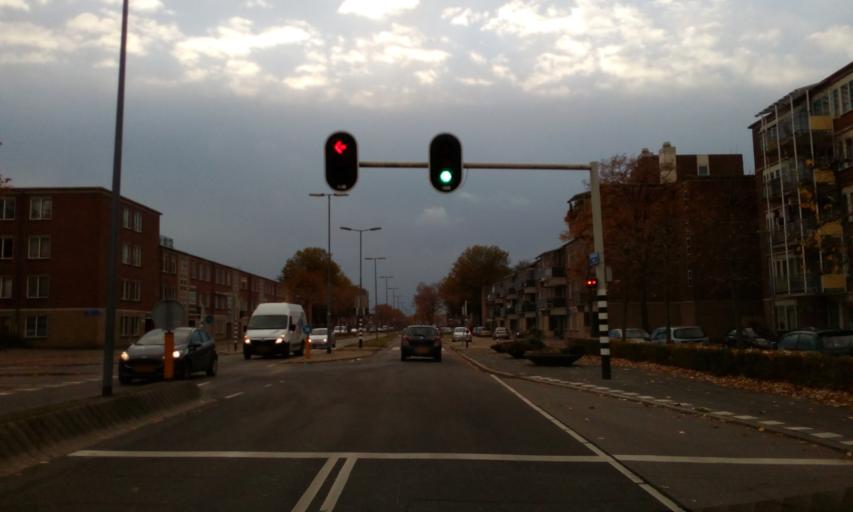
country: NL
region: South Holland
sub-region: Gemeente Capelle aan den IJssel
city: Capelle aan den IJssel
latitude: 51.9668
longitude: 4.5781
